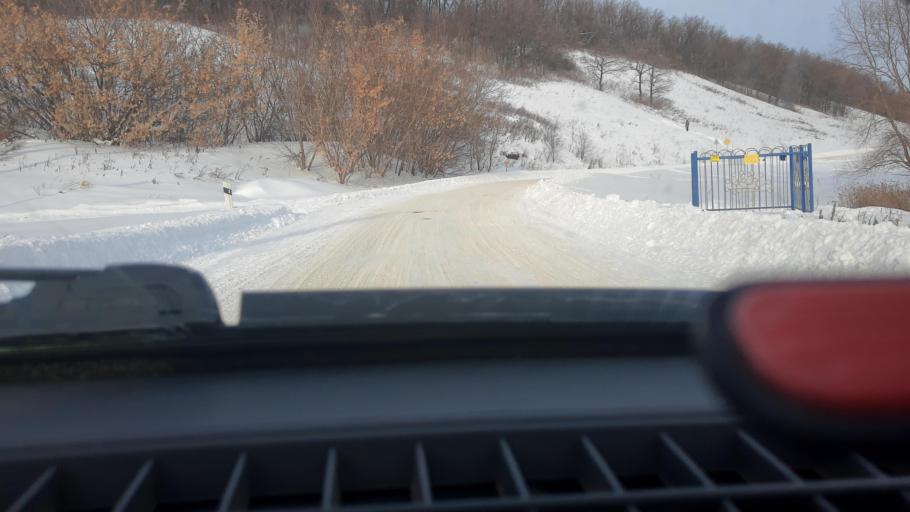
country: RU
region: Bashkortostan
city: Ufa
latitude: 54.5233
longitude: 55.9087
